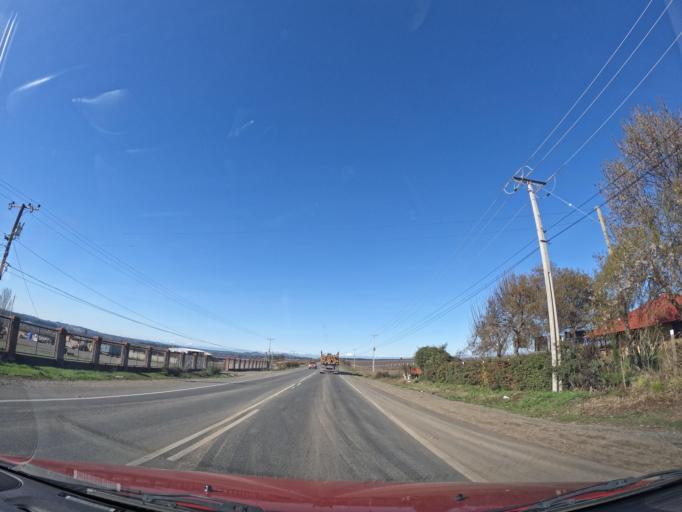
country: CL
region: Maule
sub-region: Provincia de Cauquenes
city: Cauquenes
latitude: -35.9625
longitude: -72.2448
